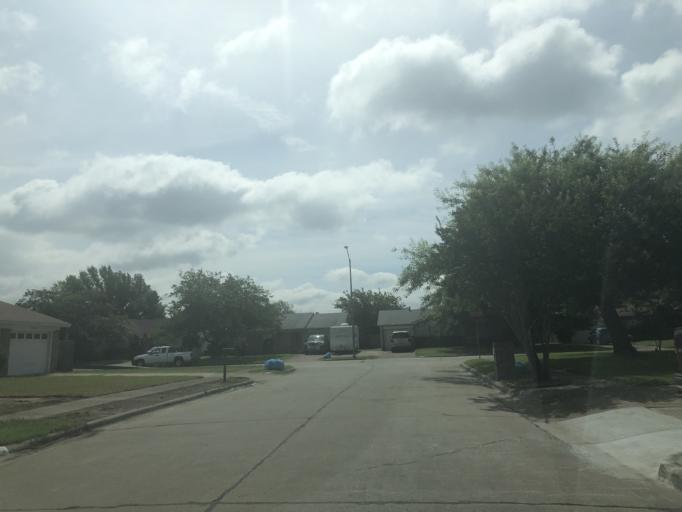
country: US
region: Texas
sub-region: Dallas County
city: Irving
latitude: 32.7956
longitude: -96.9714
